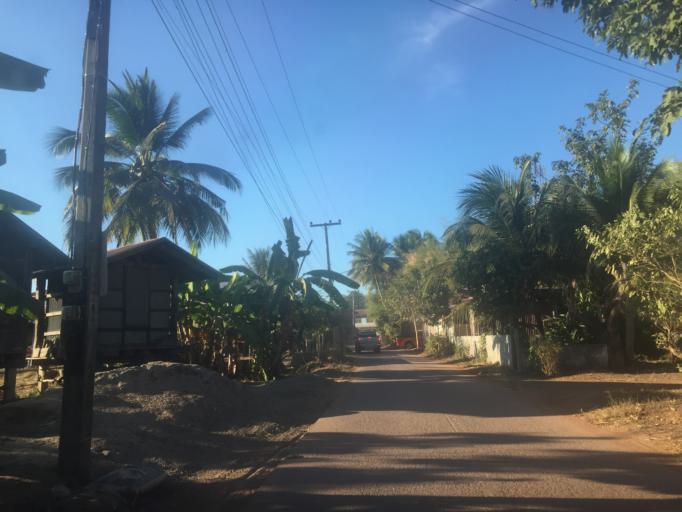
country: TH
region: Kalasin
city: Tha Khantho
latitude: 16.9837
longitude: 103.2636
